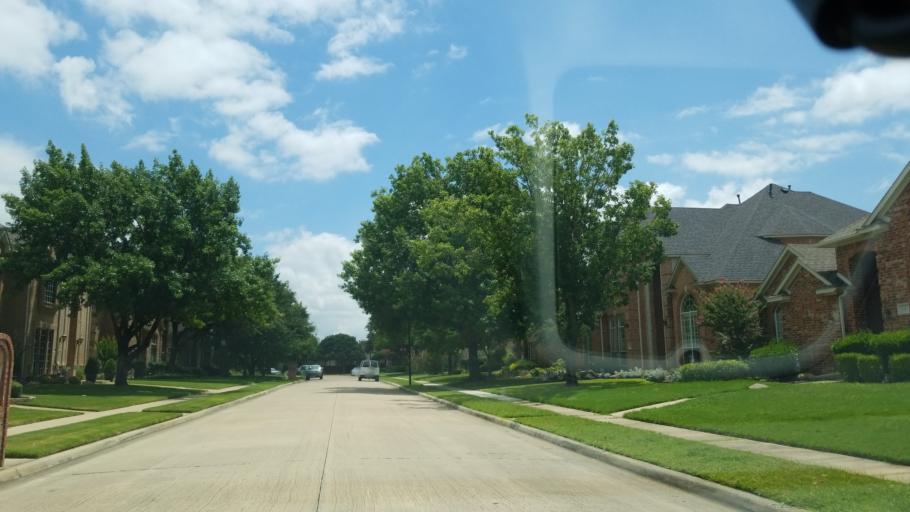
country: US
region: Texas
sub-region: Dallas County
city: Carrollton
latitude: 32.9573
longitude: -96.9517
